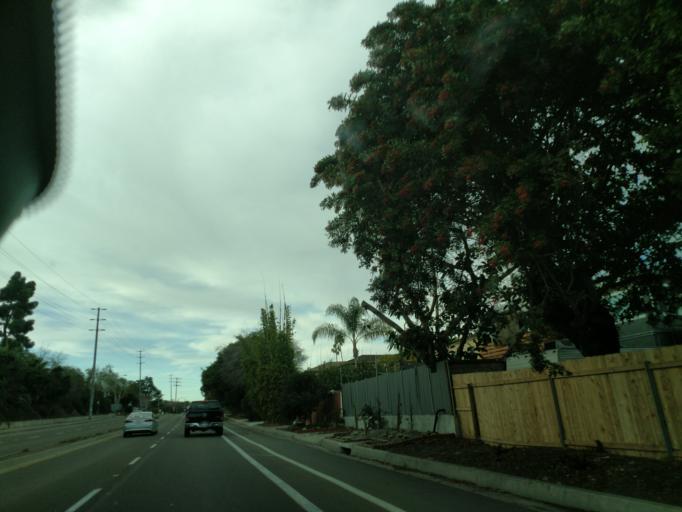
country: US
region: California
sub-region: San Diego County
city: Coronado
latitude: 32.7342
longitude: -117.2290
